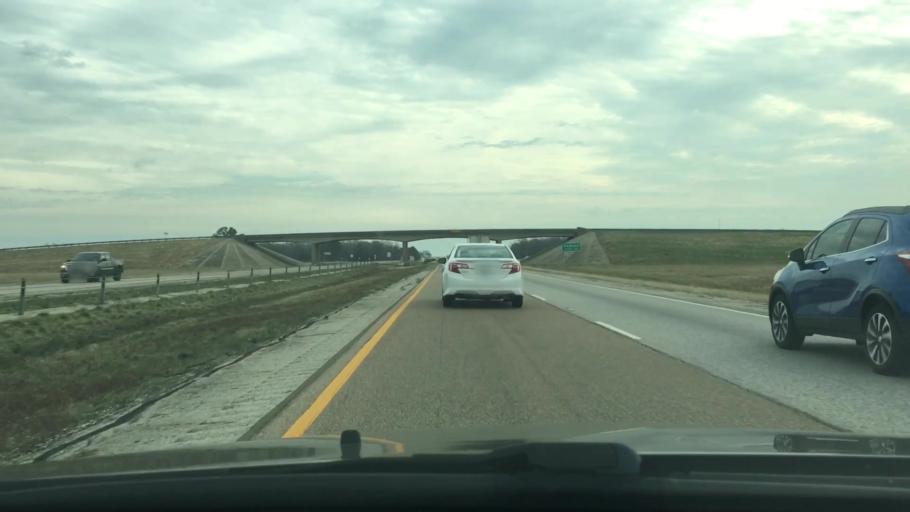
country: US
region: Texas
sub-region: Madison County
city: Madisonville
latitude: 31.0939
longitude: -95.9616
